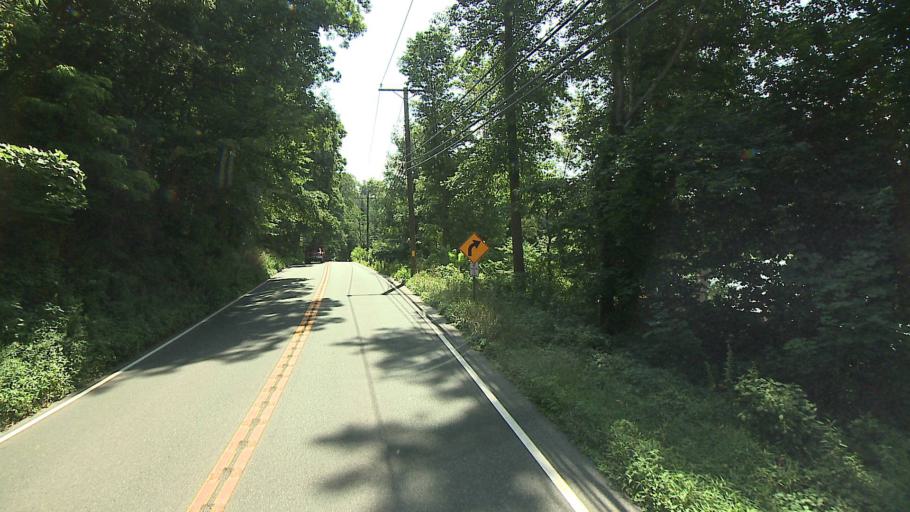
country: US
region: Connecticut
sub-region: Fairfield County
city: Sherman
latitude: 41.5164
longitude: -73.4751
